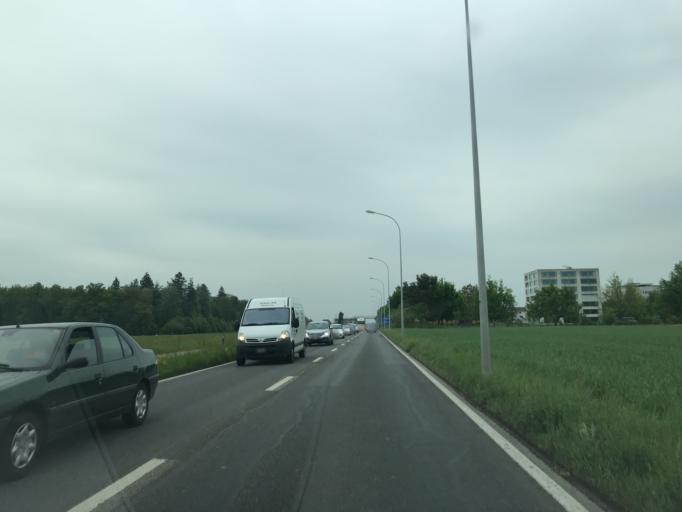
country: CH
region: Bern
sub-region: Oberaargau
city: Aarwangen
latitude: 47.2205
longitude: 7.7723
